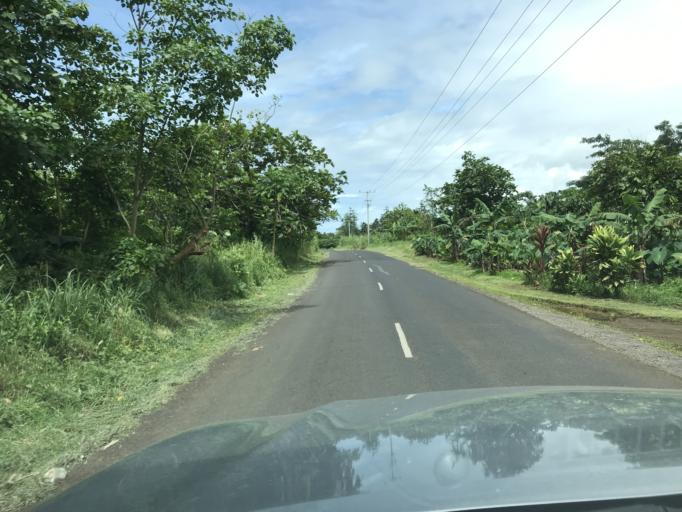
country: WS
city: Fasito`outa
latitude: -13.8591
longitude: -171.9073
